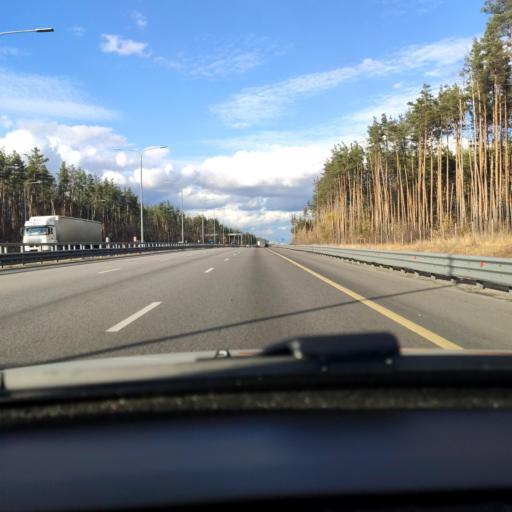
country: RU
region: Voronezj
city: Somovo
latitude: 51.6940
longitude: 39.3036
